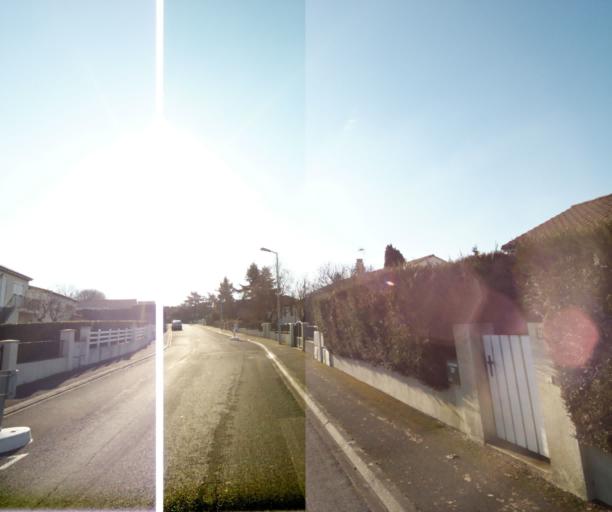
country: FR
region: Poitou-Charentes
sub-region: Departement des Deux-Sevres
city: Niort
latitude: 46.3436
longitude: -0.4477
